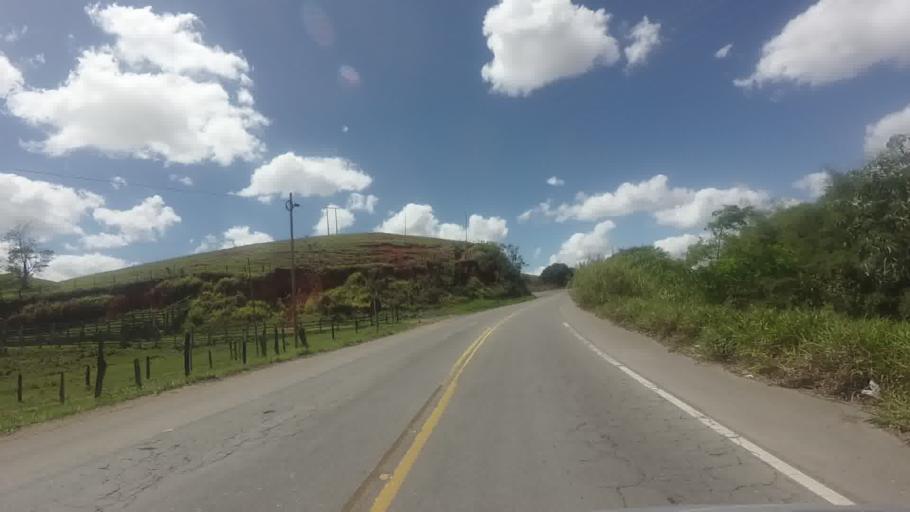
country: BR
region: Rio de Janeiro
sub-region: Santo Antonio De Padua
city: Santo Antonio de Padua
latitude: -21.6547
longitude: -42.3016
